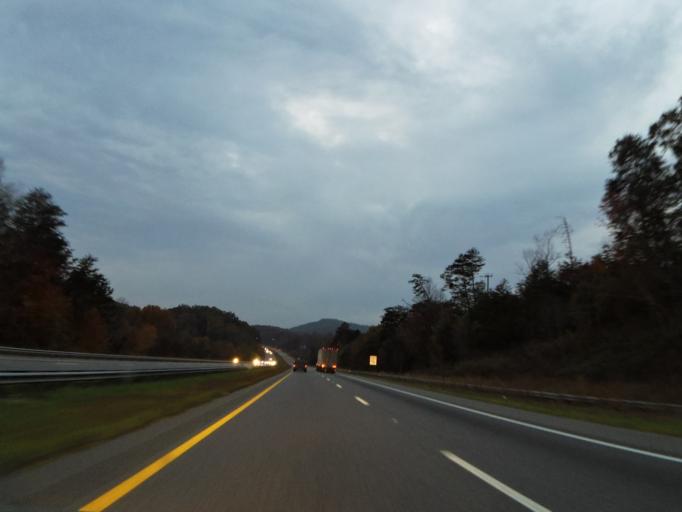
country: US
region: North Carolina
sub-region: McDowell County
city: Marion
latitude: 35.6841
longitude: -81.9238
